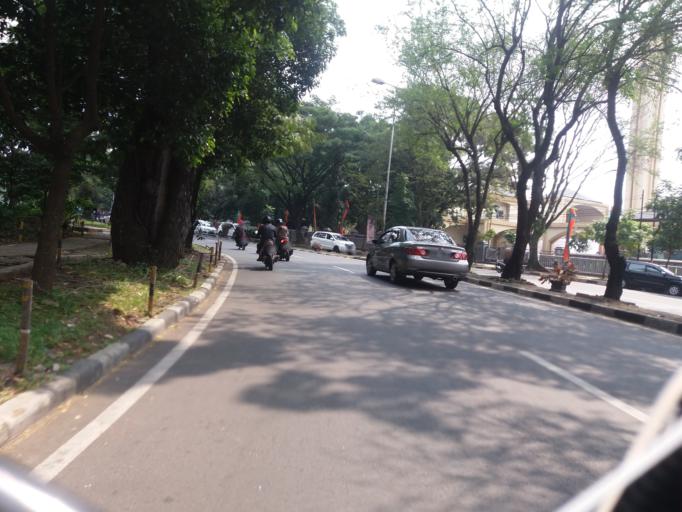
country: ID
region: West Java
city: Bandung
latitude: -6.9012
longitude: 107.6263
